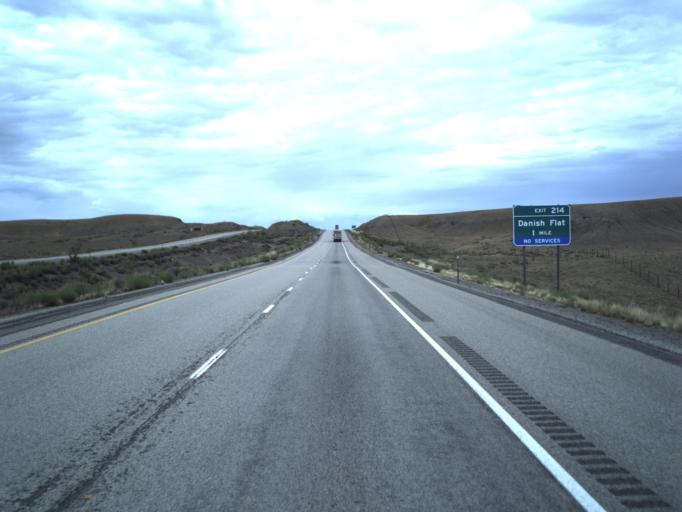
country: US
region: Utah
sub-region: Grand County
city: Moab
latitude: 39.0217
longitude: -109.2975
